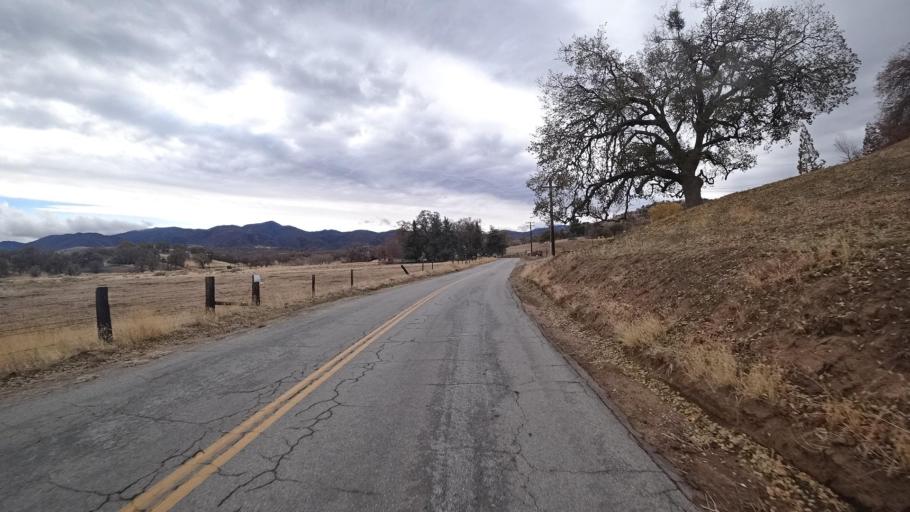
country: US
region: California
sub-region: Kern County
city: Golden Hills
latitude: 35.1311
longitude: -118.5071
